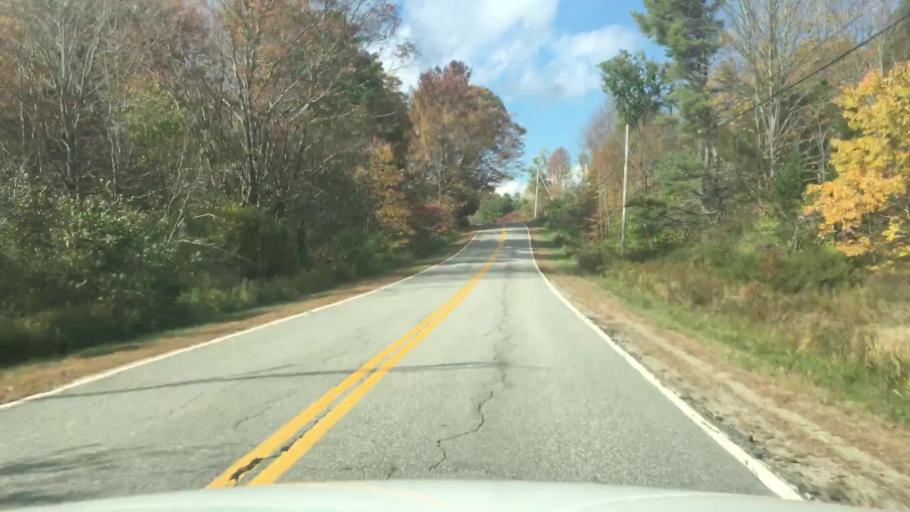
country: US
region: Maine
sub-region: Knox County
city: Washington
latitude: 44.3171
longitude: -69.3557
